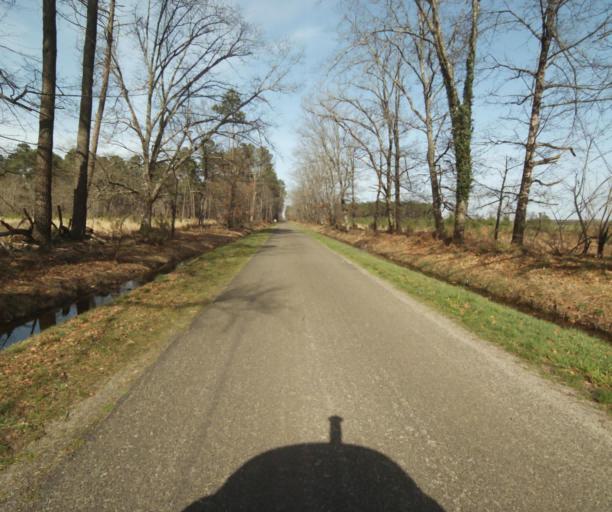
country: FR
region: Aquitaine
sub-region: Departement des Landes
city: Roquefort
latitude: 44.1545
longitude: -0.1703
